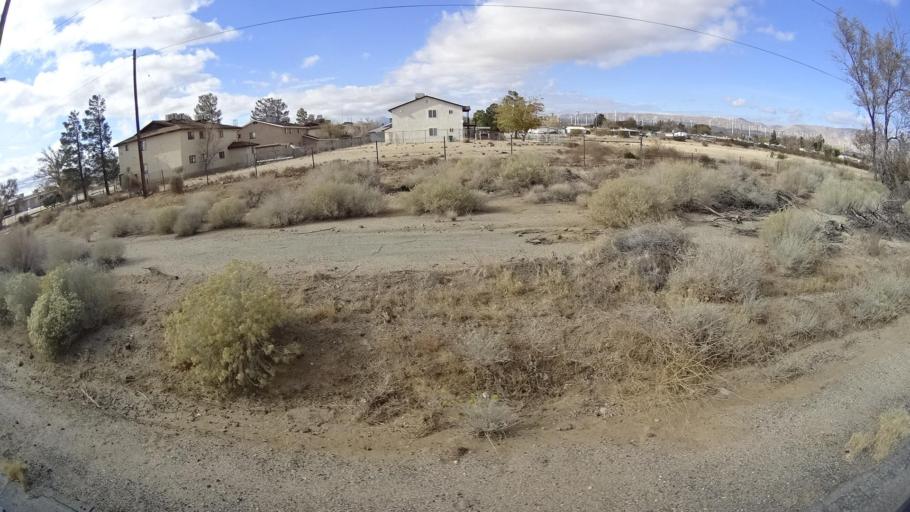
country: US
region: California
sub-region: Kern County
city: Mojave
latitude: 35.0508
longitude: -118.1855
